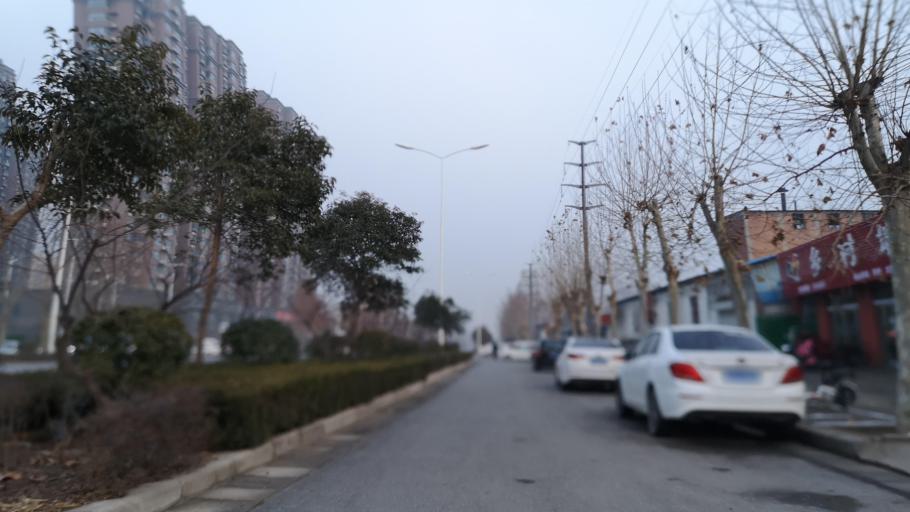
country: CN
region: Henan Sheng
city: Zhongyuanlu
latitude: 35.7473
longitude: 115.0583
